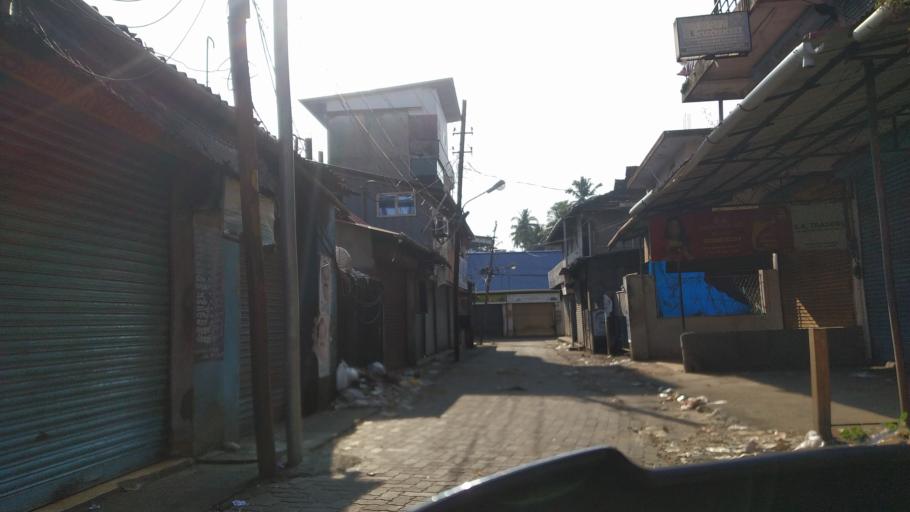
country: IN
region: Kerala
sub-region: Ernakulam
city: Cochin
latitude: 9.9811
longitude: 76.2789
